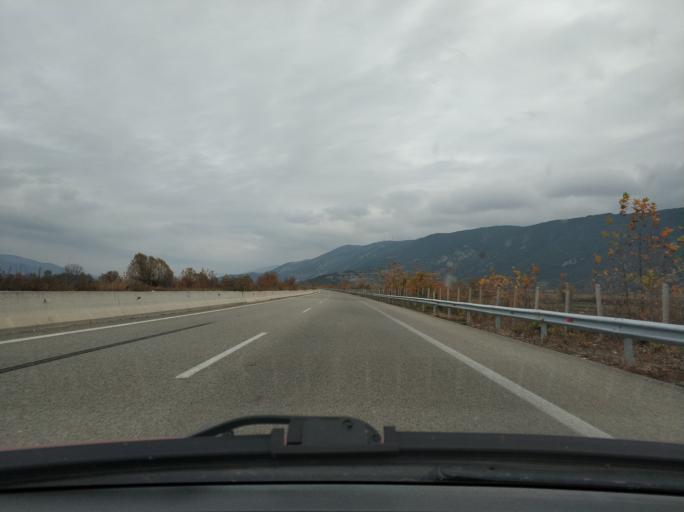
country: GR
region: East Macedonia and Thrace
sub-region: Nomos Kavalas
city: Nikisiani
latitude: 40.8243
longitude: 24.0817
